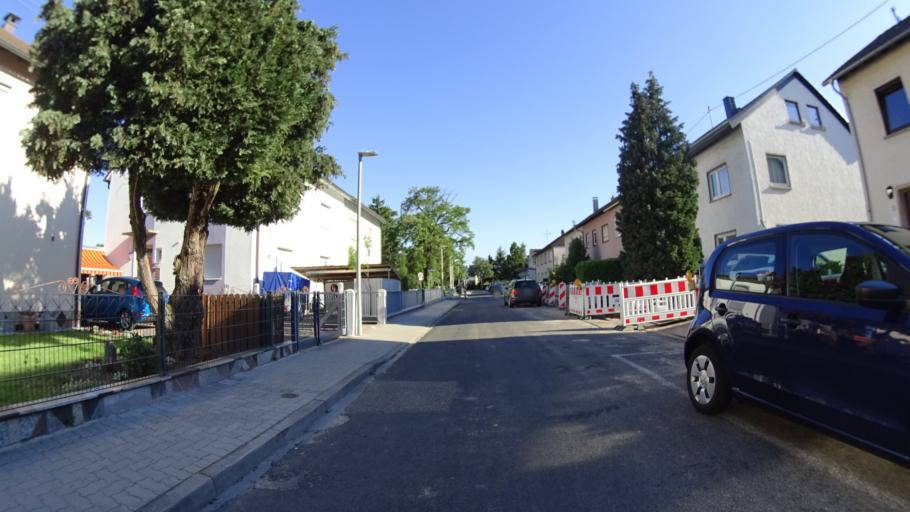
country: DE
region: Baden-Wuerttemberg
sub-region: Karlsruhe Region
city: Karlsruhe
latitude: 49.0319
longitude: 8.3684
